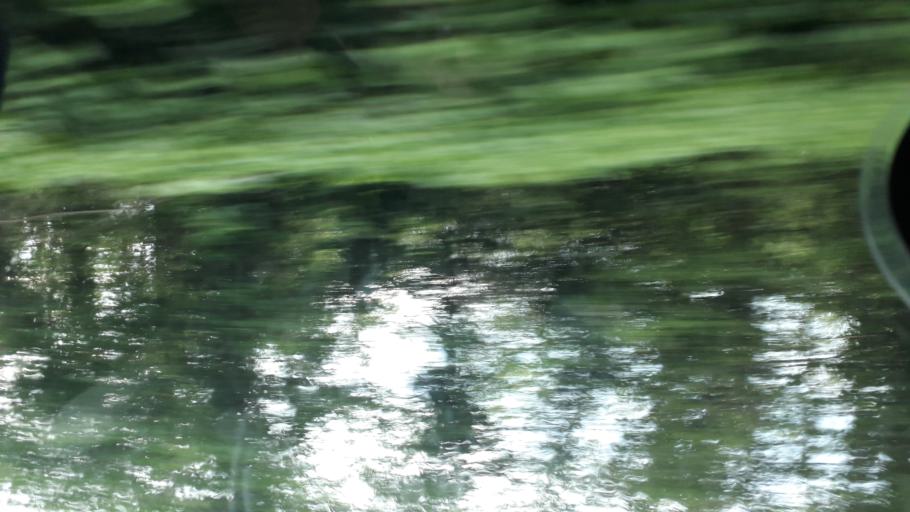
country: IE
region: Leinster
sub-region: Kildare
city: Celbridge
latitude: 53.3063
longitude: -6.5571
